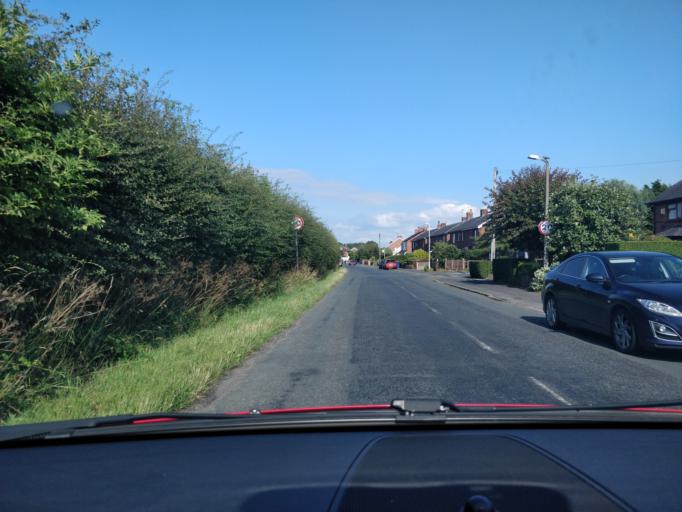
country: GB
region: England
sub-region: Lancashire
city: Banks
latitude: 53.6772
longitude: -2.9310
